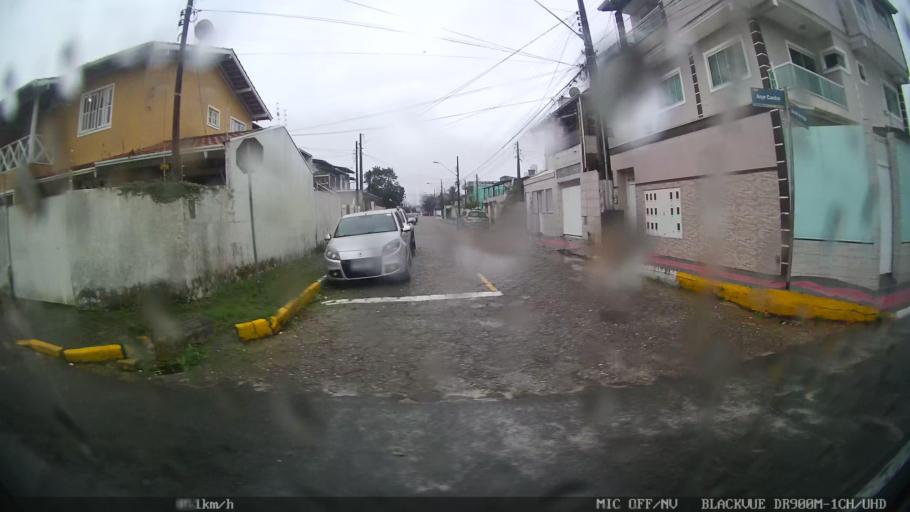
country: BR
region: Santa Catarina
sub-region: Itajai
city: Itajai
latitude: -26.9192
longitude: -48.6750
